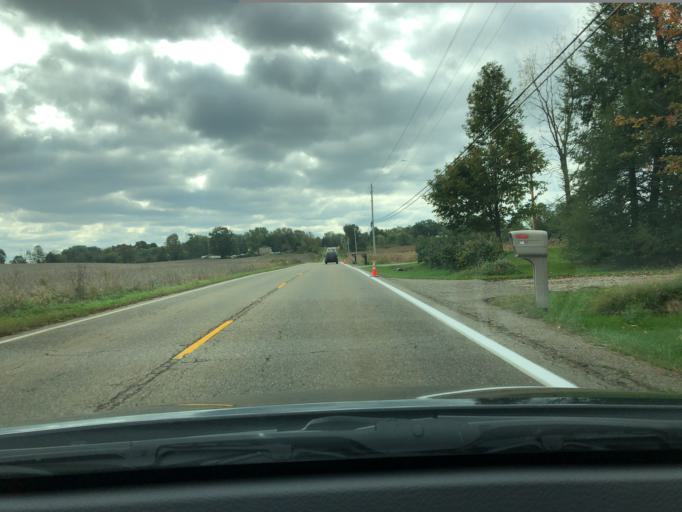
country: US
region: Ohio
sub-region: Stark County
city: Canal Fulton
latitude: 40.8509
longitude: -81.6034
